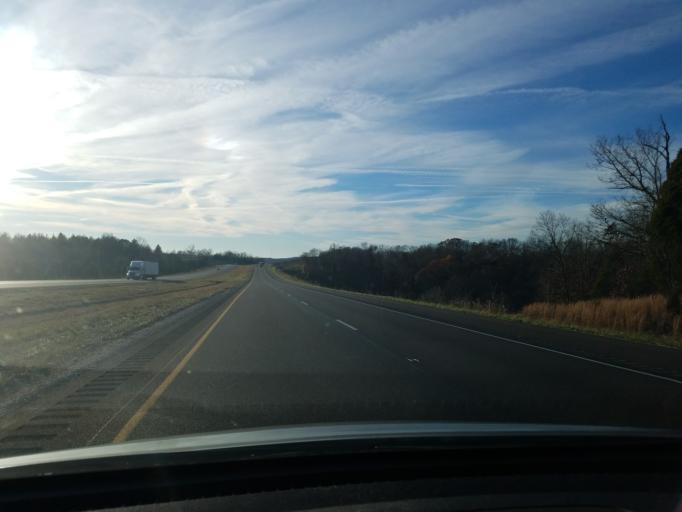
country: US
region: Indiana
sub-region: Crawford County
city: English
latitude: 38.2448
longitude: -86.4327
